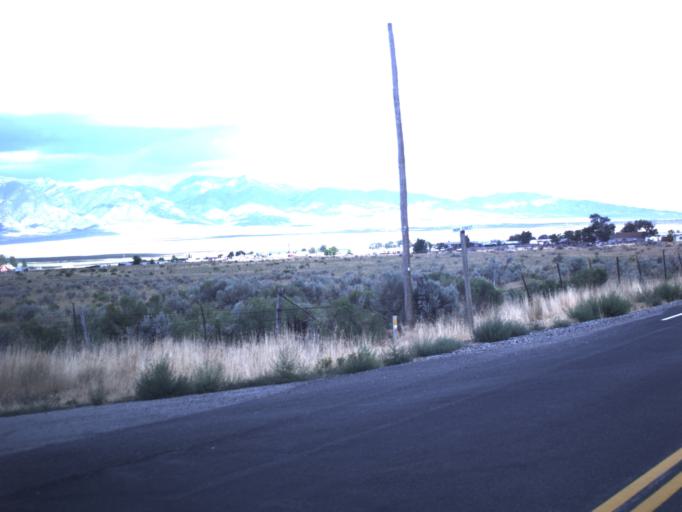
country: US
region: Utah
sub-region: Tooele County
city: Tooele
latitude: 40.3379
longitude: -112.4610
